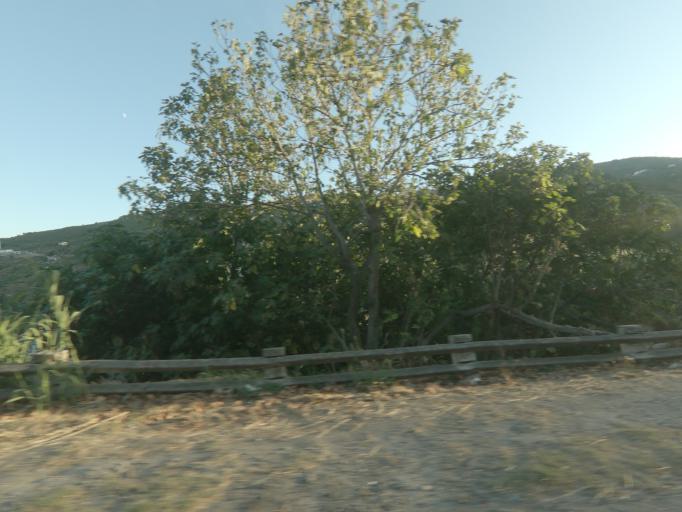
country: PT
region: Vila Real
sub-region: Peso da Regua
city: Godim
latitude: 41.1532
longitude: -7.8289
